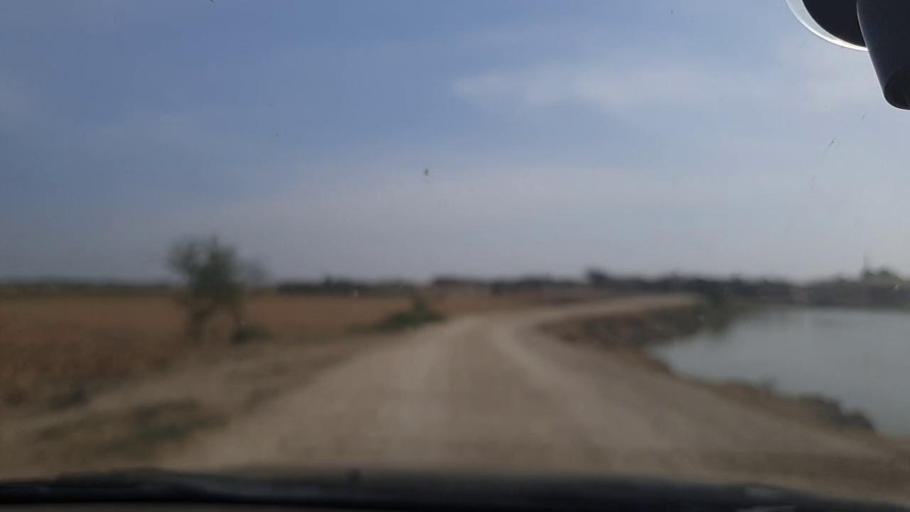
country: PK
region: Sindh
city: Mirpur Batoro
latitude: 24.7454
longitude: 68.2708
